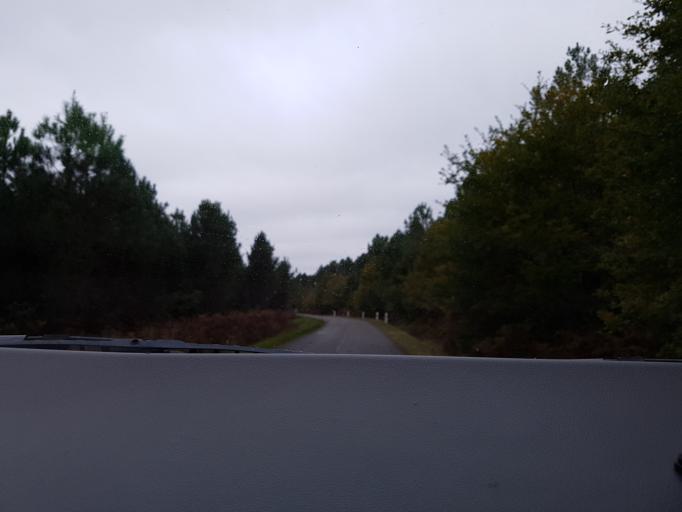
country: FR
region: Aquitaine
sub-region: Departement des Landes
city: Roquefort
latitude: 44.0807
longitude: -0.3792
